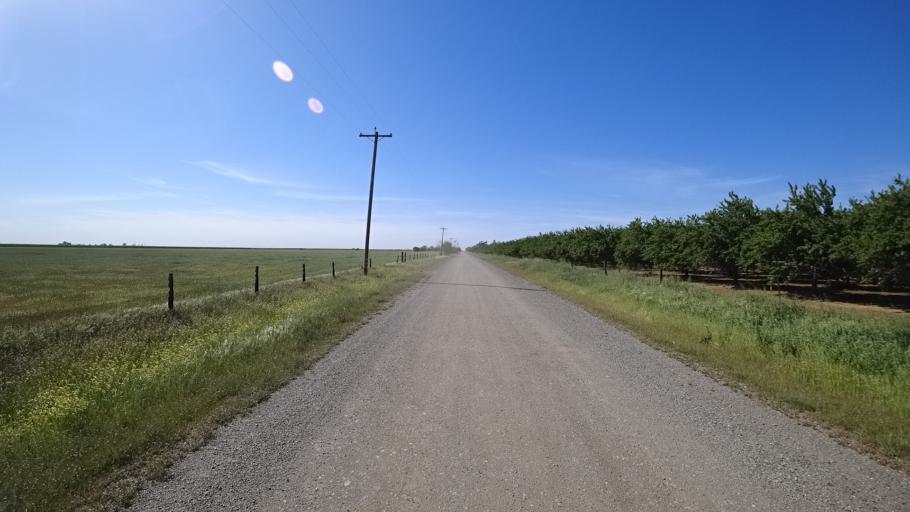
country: US
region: California
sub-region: Glenn County
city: Orland
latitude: 39.6507
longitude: -122.1597
